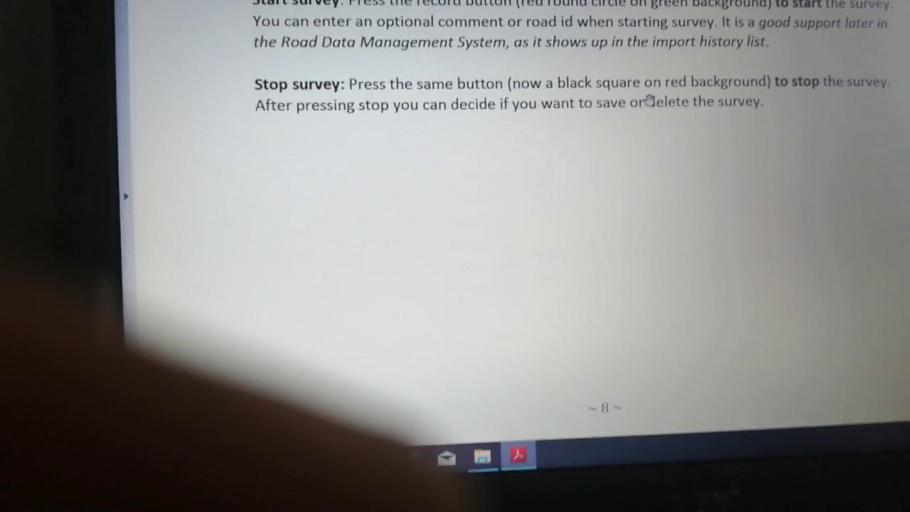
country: RS
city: Veternik
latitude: 45.2416
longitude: 19.7940
